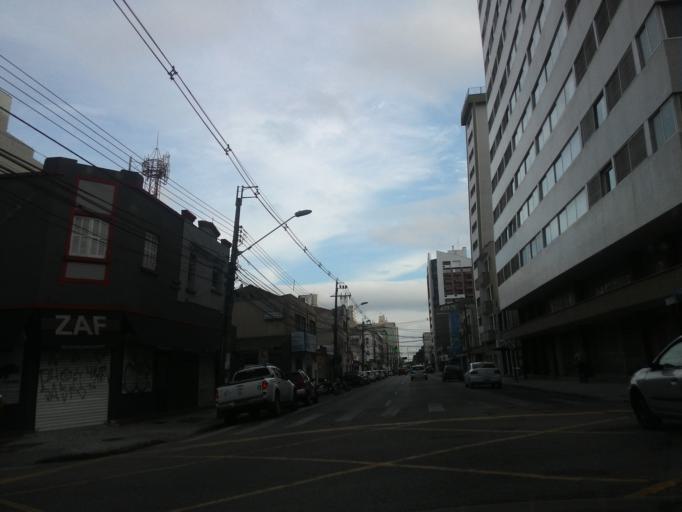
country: BR
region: Parana
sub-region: Curitiba
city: Curitiba
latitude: -25.4300
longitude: -49.2637
